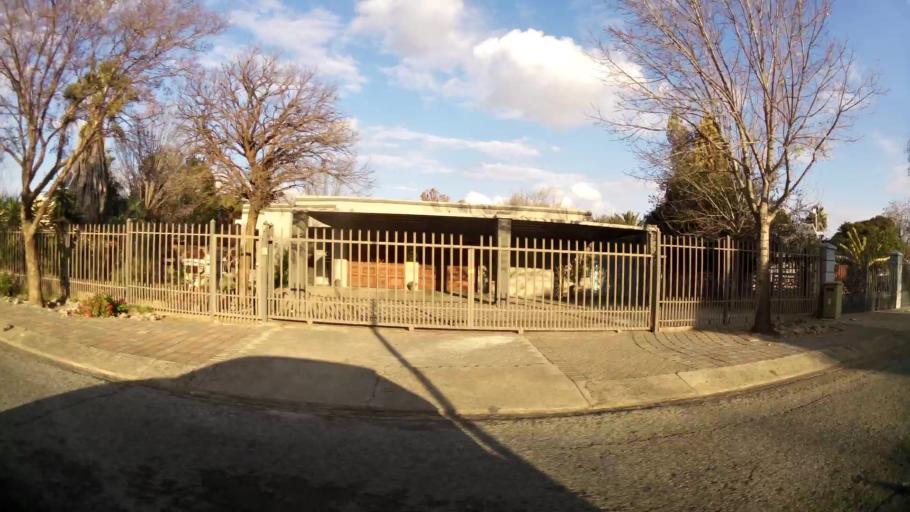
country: ZA
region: Orange Free State
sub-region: Mangaung Metropolitan Municipality
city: Bloemfontein
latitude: -29.1457
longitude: 26.1847
